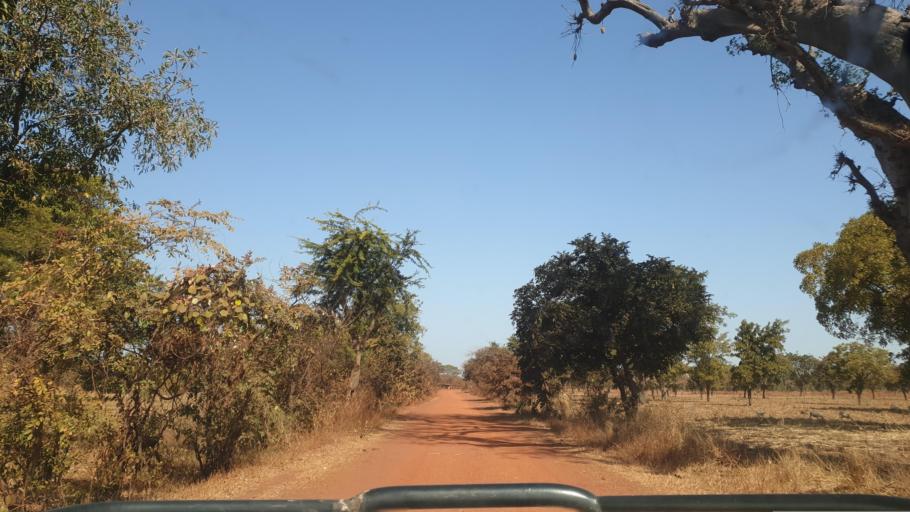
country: ML
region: Sikasso
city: Bougouni
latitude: 11.8447
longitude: -6.9784
